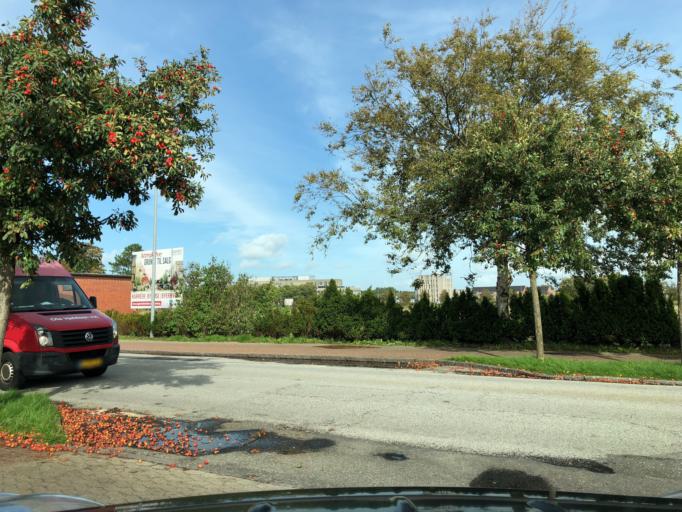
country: DK
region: Central Jutland
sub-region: Holstebro Kommune
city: Holstebro
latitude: 56.3685
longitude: 8.6173
